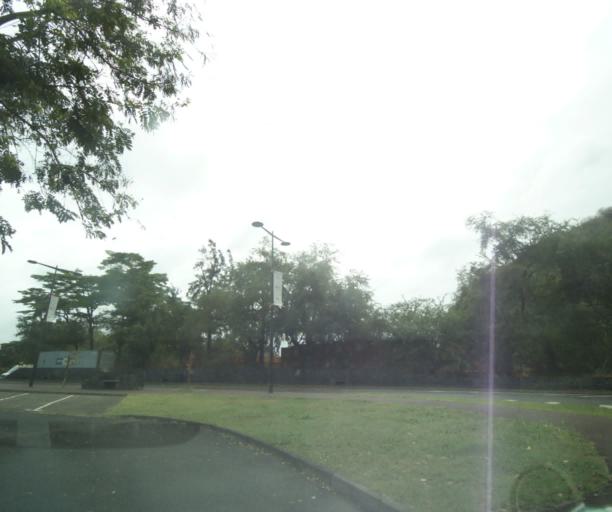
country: RE
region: Reunion
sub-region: Reunion
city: Saint-Paul
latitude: -21.0162
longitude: 55.2609
